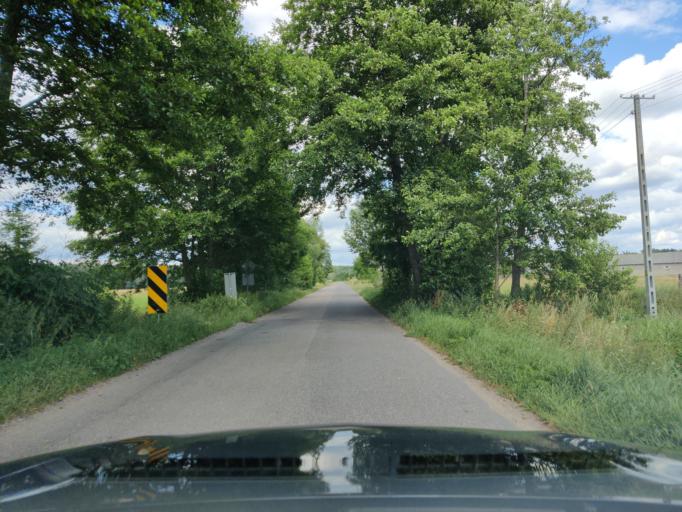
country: PL
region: Masovian Voivodeship
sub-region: Powiat wegrowski
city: Miedzna
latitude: 52.4864
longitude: 22.0220
